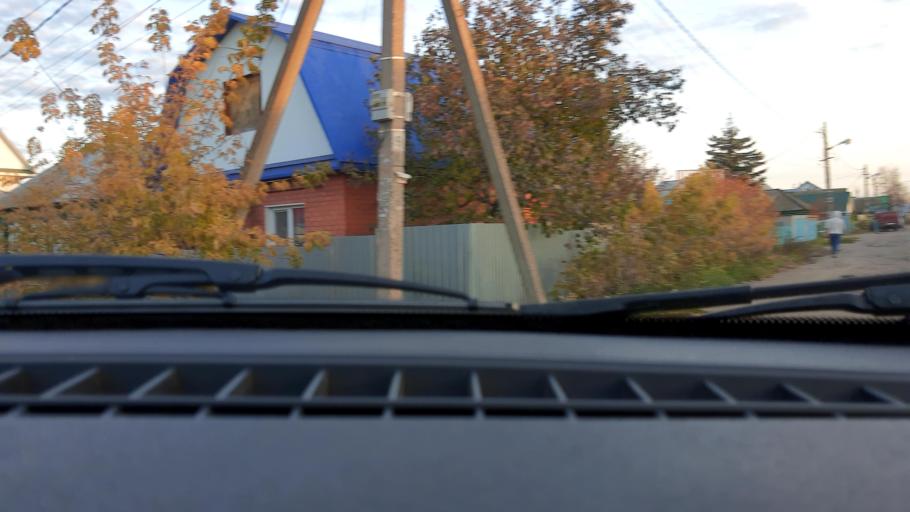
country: RU
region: Bashkortostan
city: Ufa
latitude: 54.7411
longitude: 55.9198
